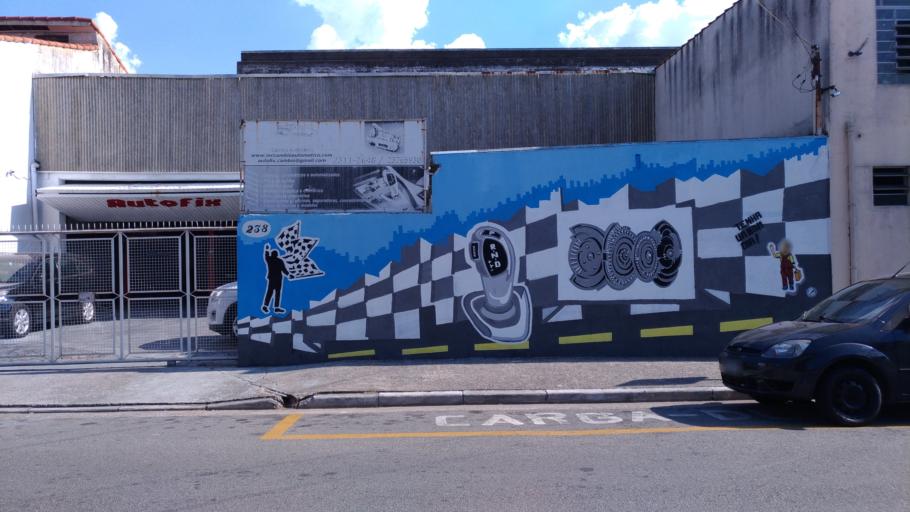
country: BR
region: Sao Paulo
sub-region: Sao Caetano Do Sul
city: Sao Caetano do Sul
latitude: -23.6226
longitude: -46.5765
